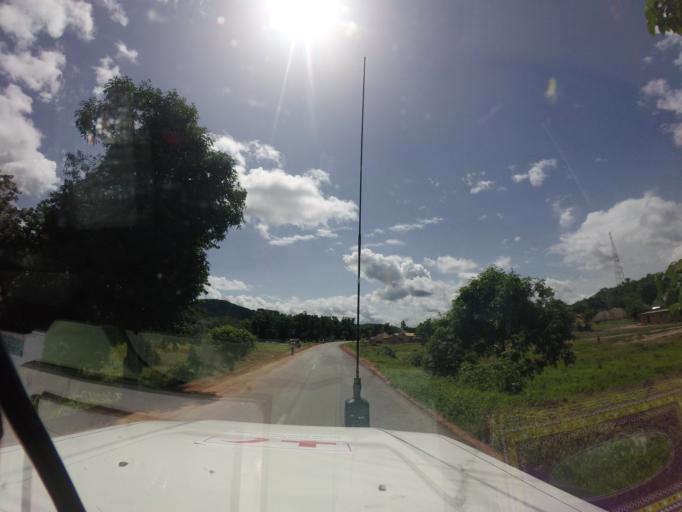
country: GN
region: Mamou
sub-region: Mamou Prefecture
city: Mamou
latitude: 10.1831
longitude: -11.8408
